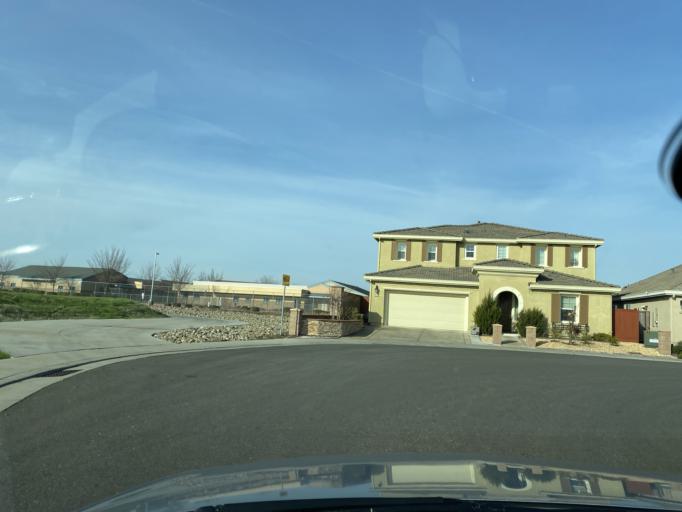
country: US
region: California
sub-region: Sacramento County
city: Elk Grove
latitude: 38.3960
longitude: -121.3946
